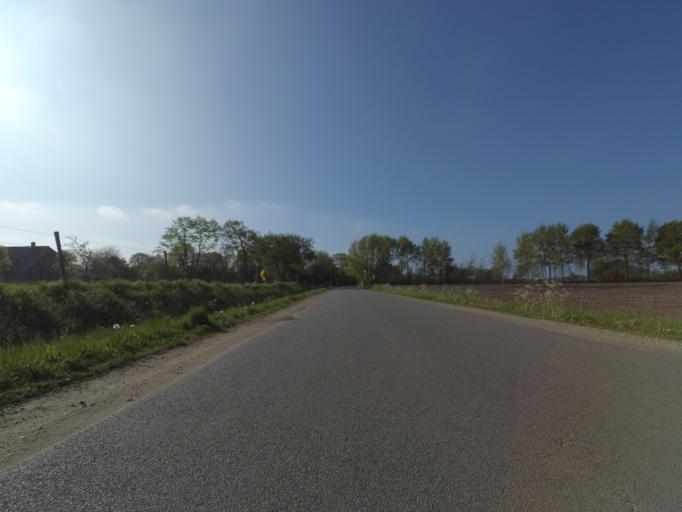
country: NL
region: Gelderland
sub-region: Gemeente Barneveld
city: Voorthuizen
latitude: 52.1786
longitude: 5.6145
